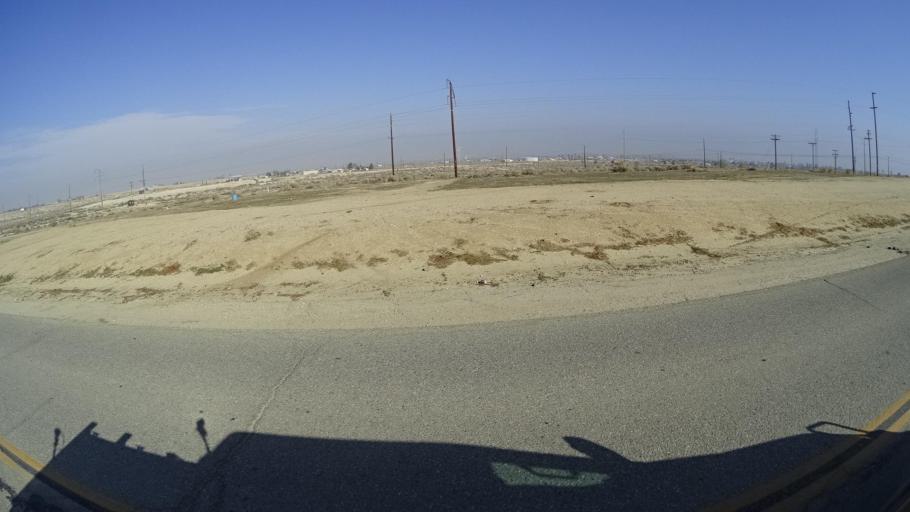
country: US
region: California
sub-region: Kern County
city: Taft Heights
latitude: 35.1387
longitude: -119.4854
